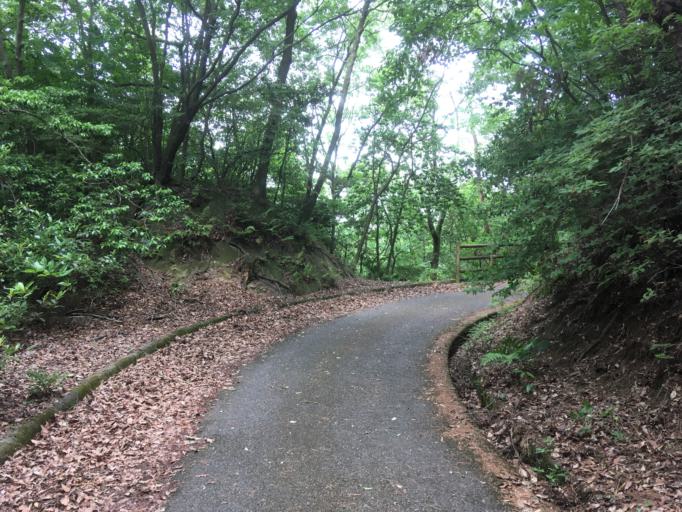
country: JP
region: Nara
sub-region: Ikoma-shi
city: Ikoma
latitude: 34.6955
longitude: 135.6712
